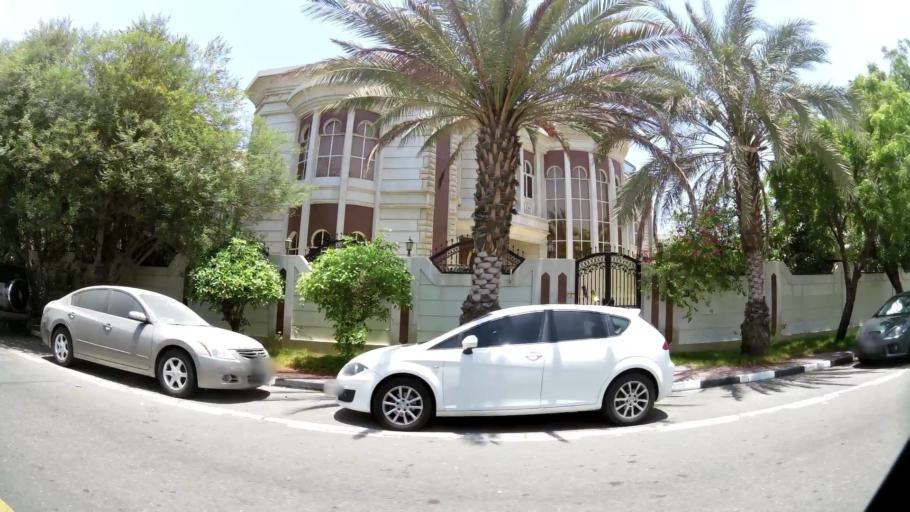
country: AE
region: Ash Shariqah
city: Sharjah
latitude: 25.2401
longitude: 55.2886
